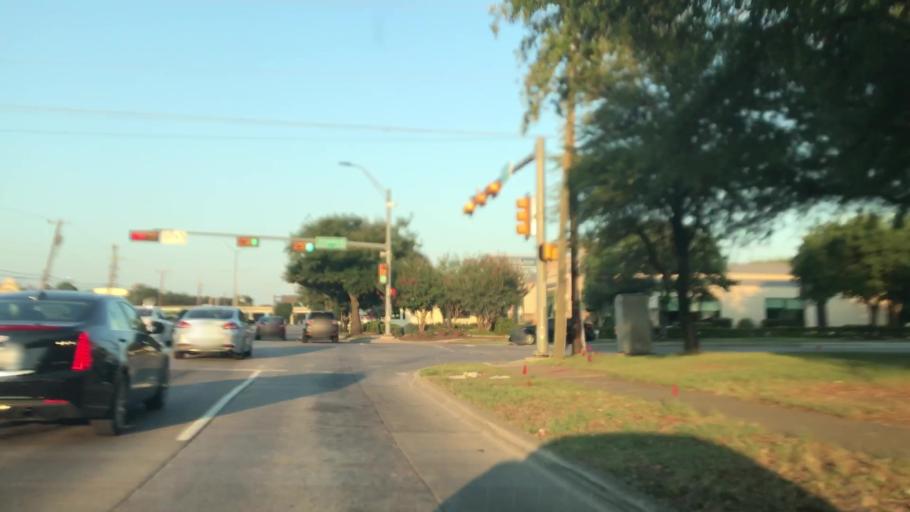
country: US
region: Texas
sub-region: Dallas County
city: Addison
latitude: 32.9094
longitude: -96.8188
